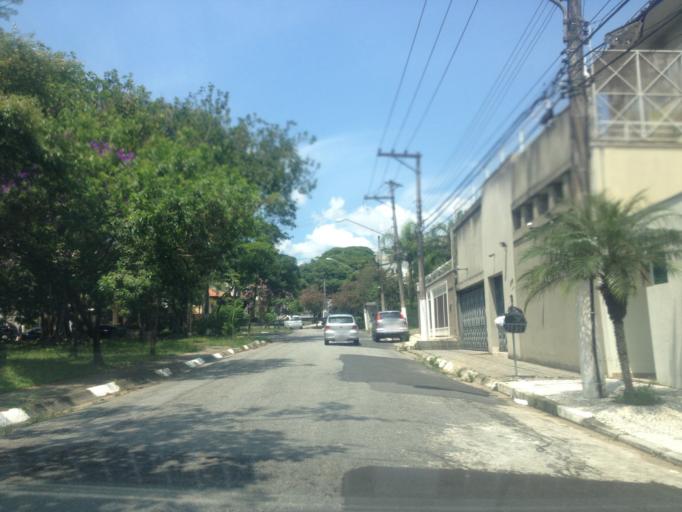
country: BR
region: Sao Paulo
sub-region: Diadema
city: Diadema
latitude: -23.6498
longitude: -46.6790
